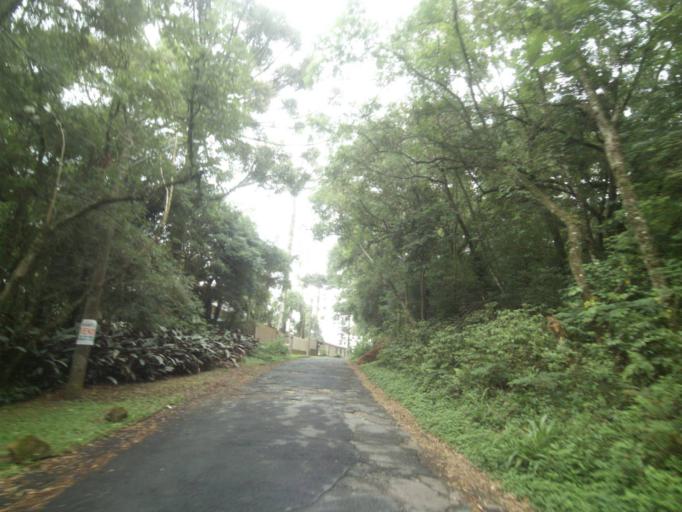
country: BR
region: Parana
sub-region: Curitiba
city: Curitiba
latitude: -25.4121
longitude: -49.3067
